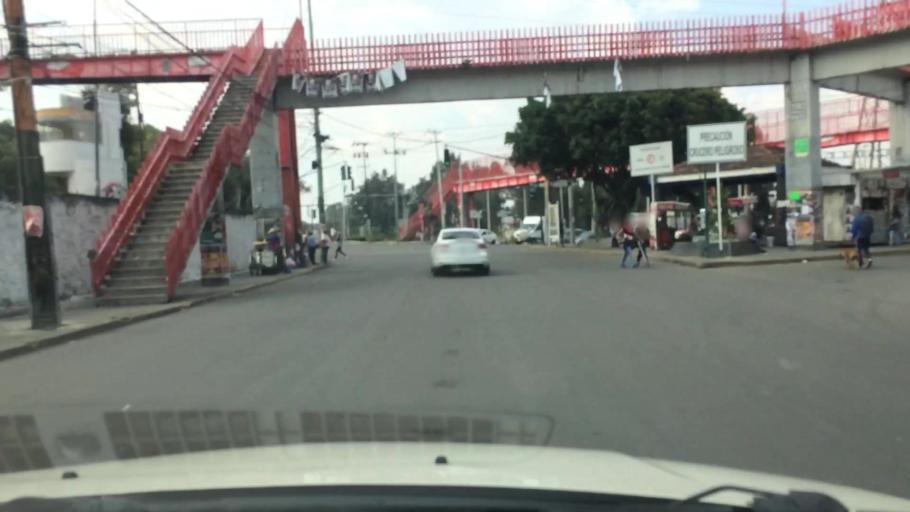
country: MX
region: Mexico City
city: Xochimilco
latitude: 19.2681
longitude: -99.1273
